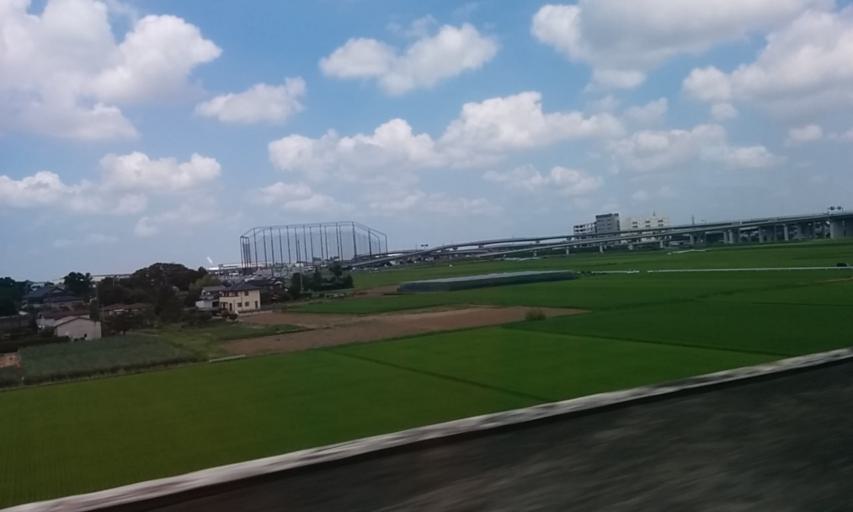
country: JP
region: Saitama
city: Shiraoka
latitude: 36.0403
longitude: 139.6651
